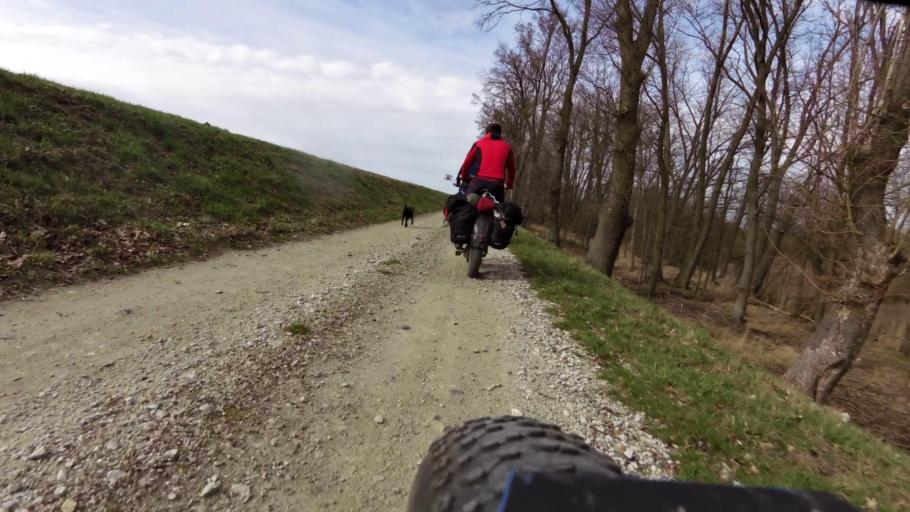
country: DE
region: Brandenburg
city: Reitwein
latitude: 52.5106
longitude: 14.6162
